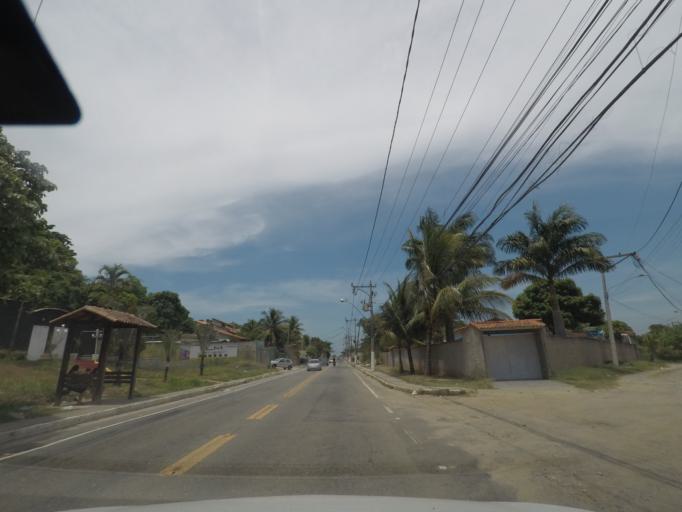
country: BR
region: Rio de Janeiro
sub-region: Marica
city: Marica
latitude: -22.9366
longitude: -42.8279
